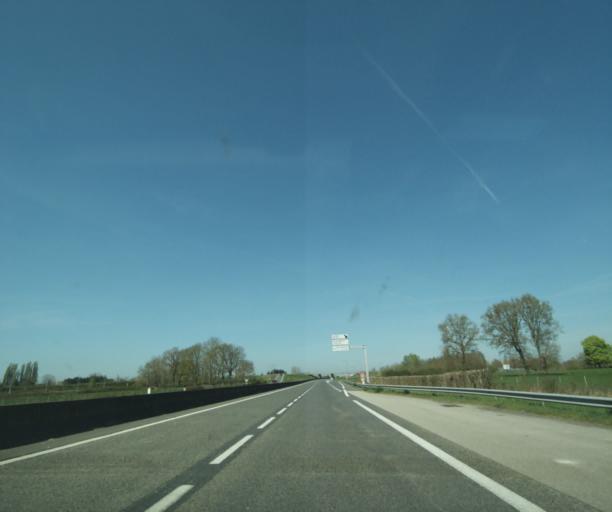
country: FR
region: Auvergne
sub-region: Departement de l'Allier
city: Avermes
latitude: 46.5959
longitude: 3.3123
